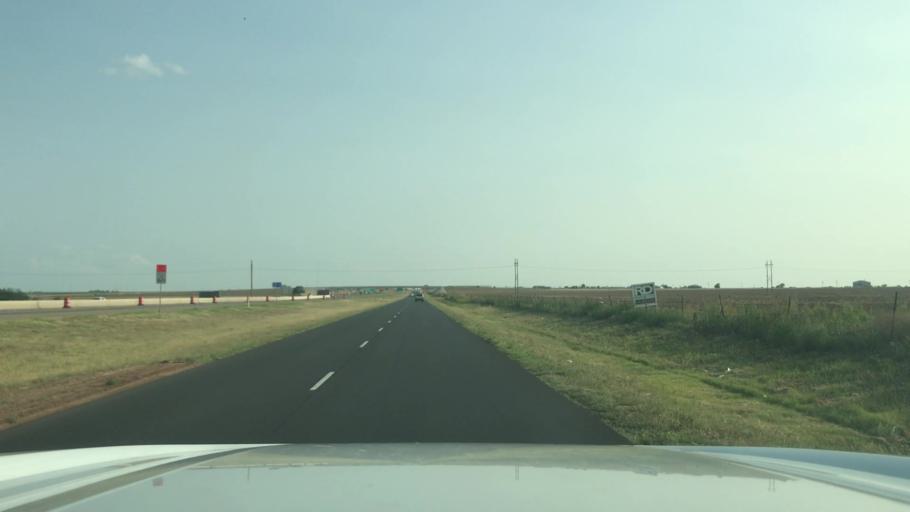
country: US
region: Texas
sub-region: Randall County
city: Canyon
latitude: 35.1101
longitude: -101.9116
